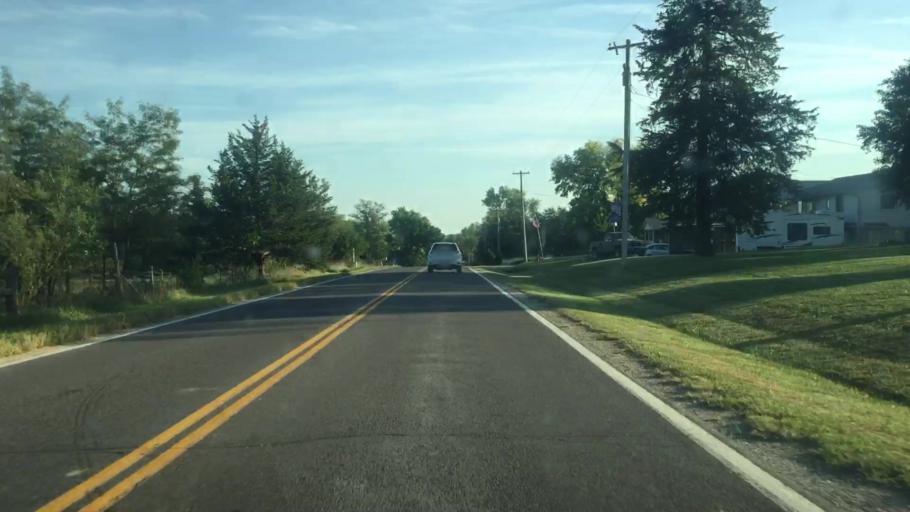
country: US
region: Kansas
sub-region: Brown County
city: Horton
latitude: 39.5553
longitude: -95.5247
